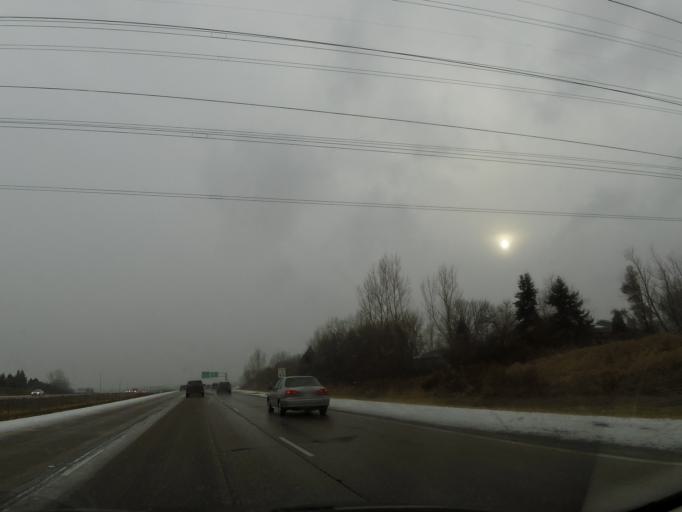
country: US
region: Minnesota
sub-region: Dakota County
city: Eagan
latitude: 44.7977
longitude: -93.2223
